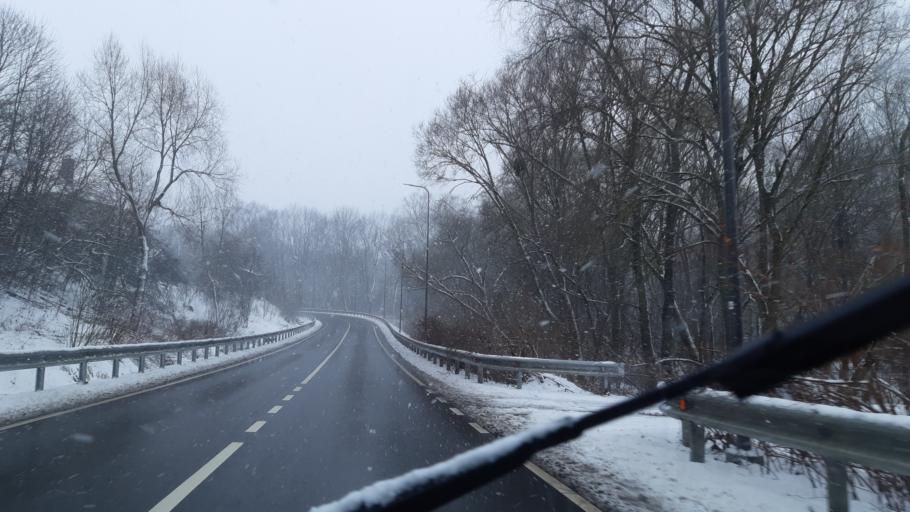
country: LT
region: Kauno apskritis
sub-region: Kaunas
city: Silainiai
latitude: 54.9321
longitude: 23.8714
